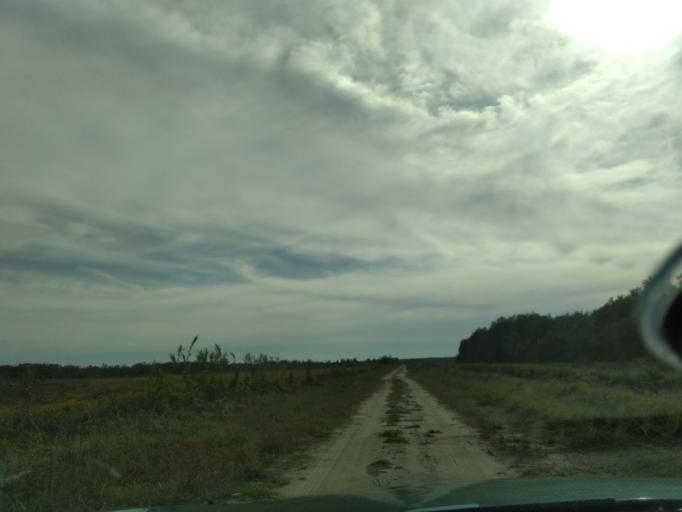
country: US
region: North Carolina
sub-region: Beaufort County
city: Belhaven
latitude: 35.7153
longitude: -76.5775
